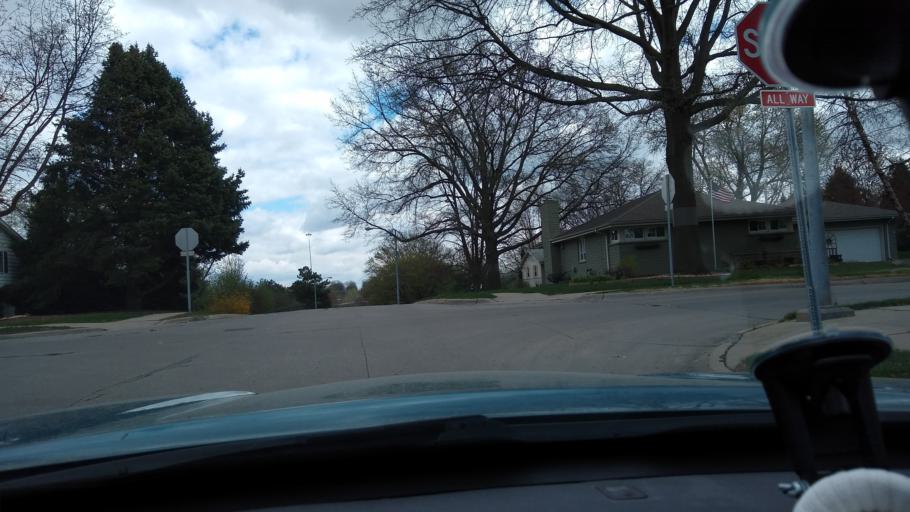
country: US
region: Nebraska
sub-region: Douglas County
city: Ralston
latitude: 41.2270
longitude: -96.0914
